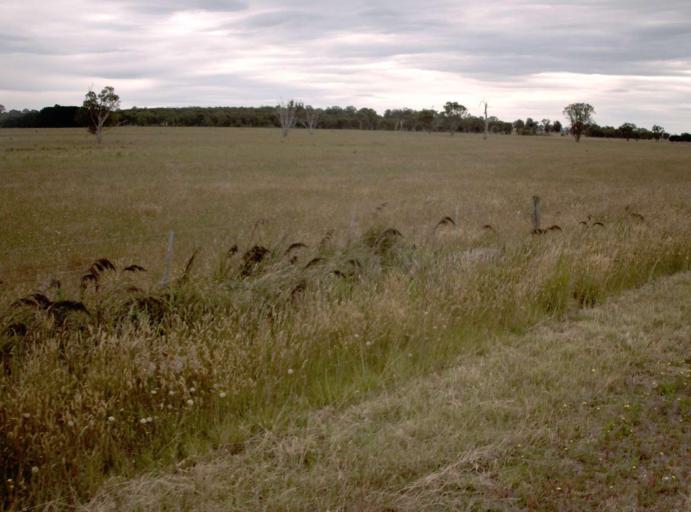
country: AU
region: Victoria
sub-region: East Gippsland
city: Bairnsdale
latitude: -37.9479
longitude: 147.5229
